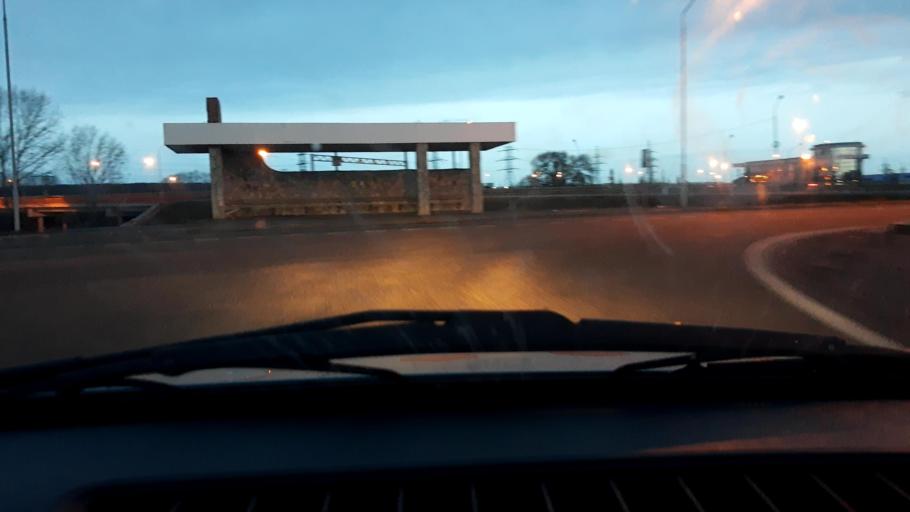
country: RU
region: Bashkortostan
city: Avdon
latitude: 54.6754
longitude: 55.8053
